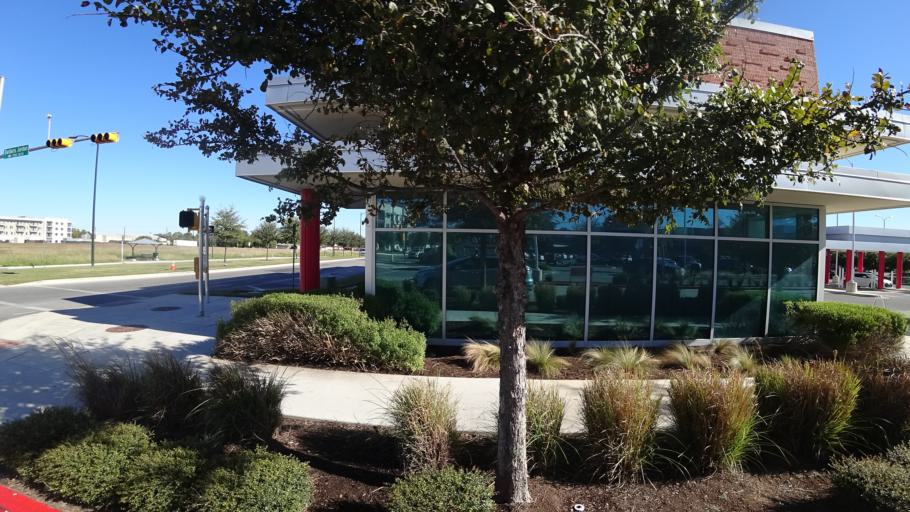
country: US
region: Texas
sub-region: Travis County
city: Austin
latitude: 30.3022
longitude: -97.6996
